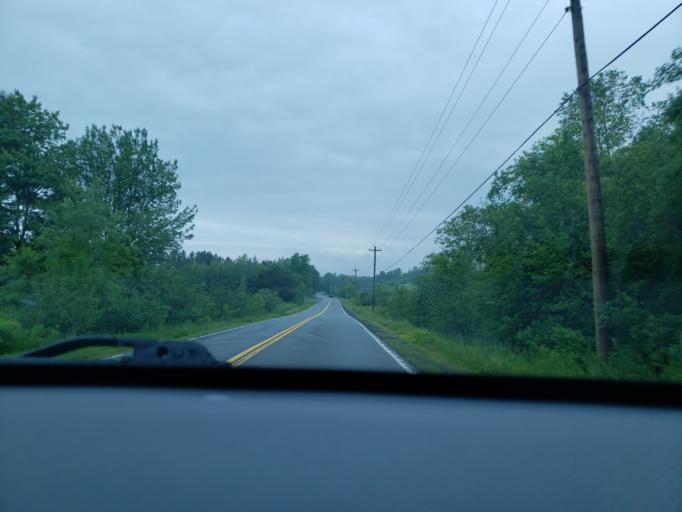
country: CA
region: Nova Scotia
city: Windsor
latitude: 45.0625
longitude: -63.9763
